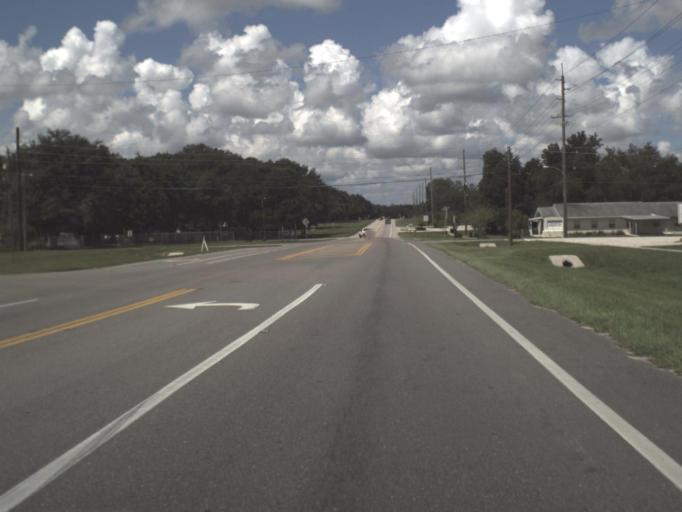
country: US
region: Florida
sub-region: Polk County
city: Polk City
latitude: 28.1792
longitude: -81.8296
